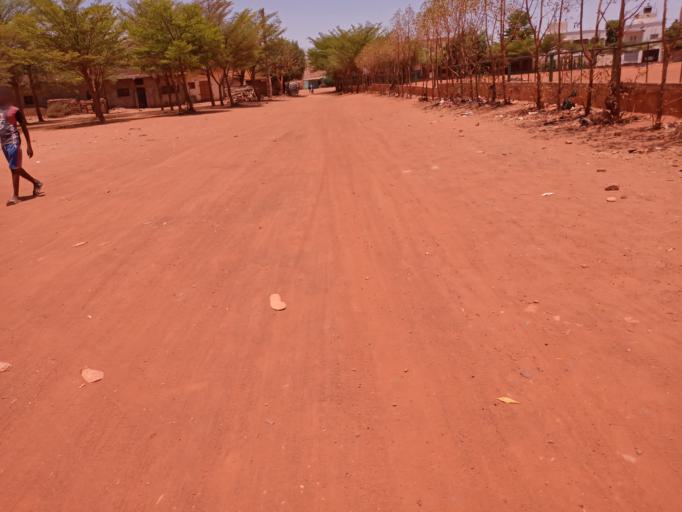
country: ML
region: Bamako
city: Bamako
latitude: 12.5816
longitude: -7.9564
